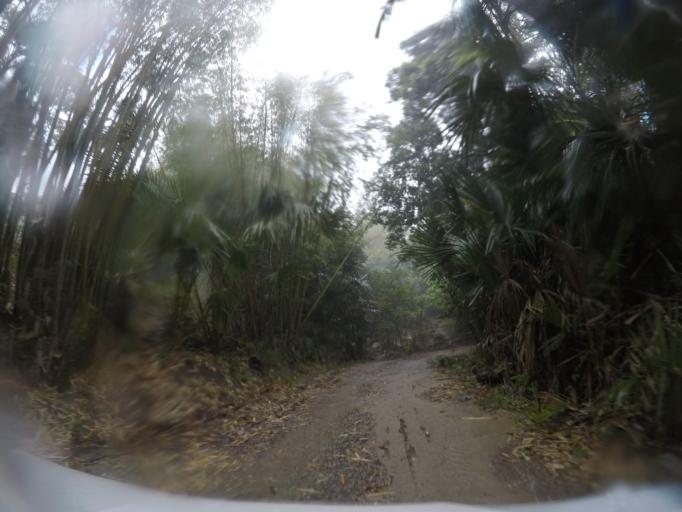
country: TL
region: Baucau
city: Venilale
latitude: -8.6350
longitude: 126.4382
